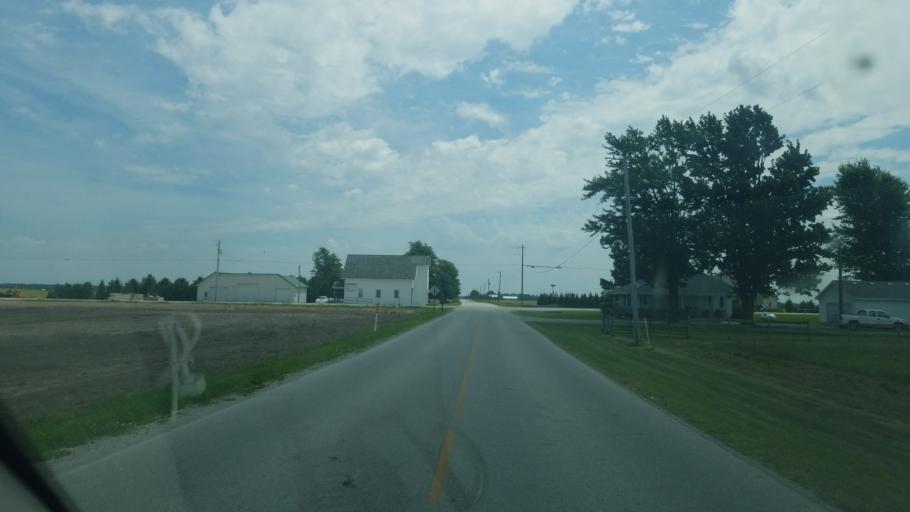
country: US
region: Ohio
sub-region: Wood County
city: Bowling Green
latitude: 41.2967
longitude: -83.5938
